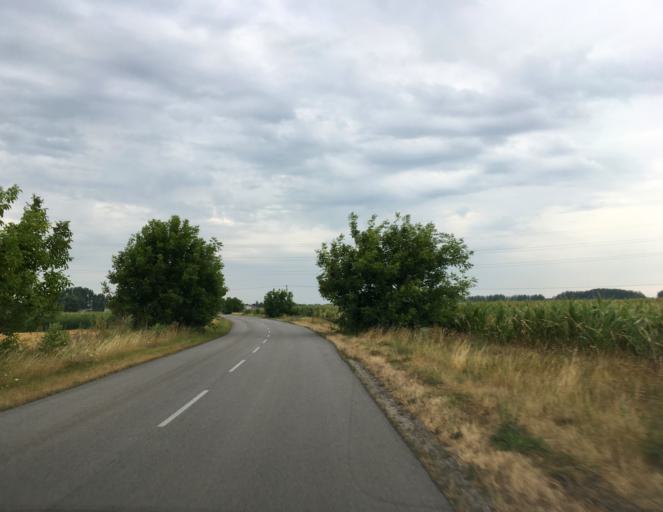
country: SK
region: Trnavsky
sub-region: Okres Dunajska Streda
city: Velky Meder
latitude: 47.9289
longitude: 17.7017
